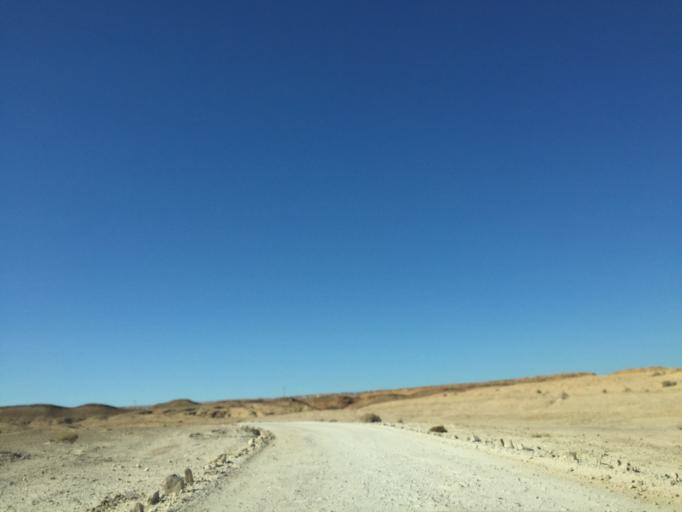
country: IL
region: Southern District
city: Mitzpe Ramon
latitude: 30.6141
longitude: 34.9072
